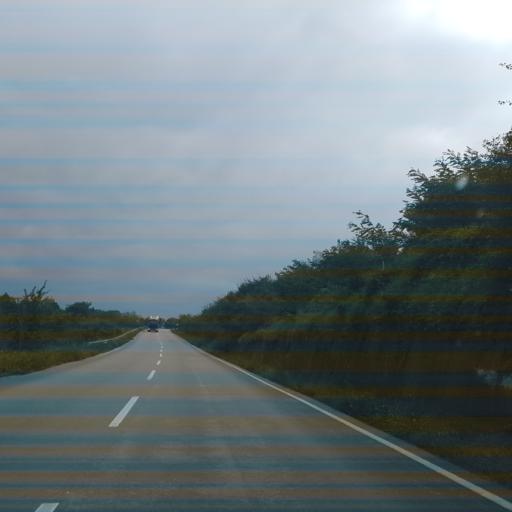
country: RS
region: Central Serbia
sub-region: Nisavski Okrug
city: Razanj
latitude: 43.6724
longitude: 21.5454
